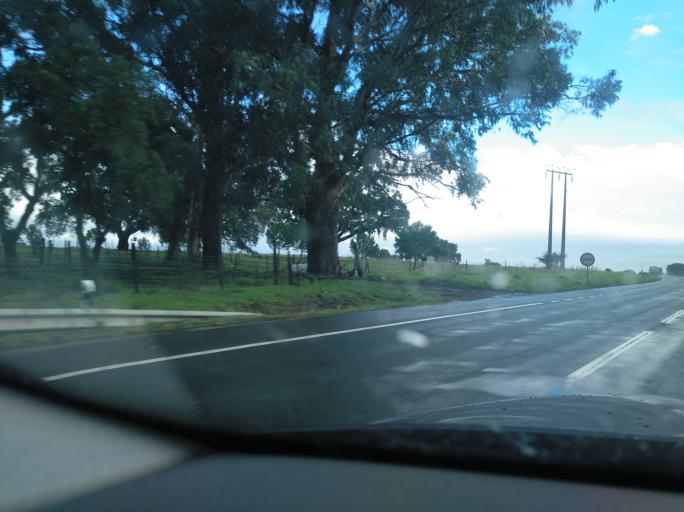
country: PT
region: Setubal
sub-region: Grandola
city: Grandola
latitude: 38.0164
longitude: -8.3963
